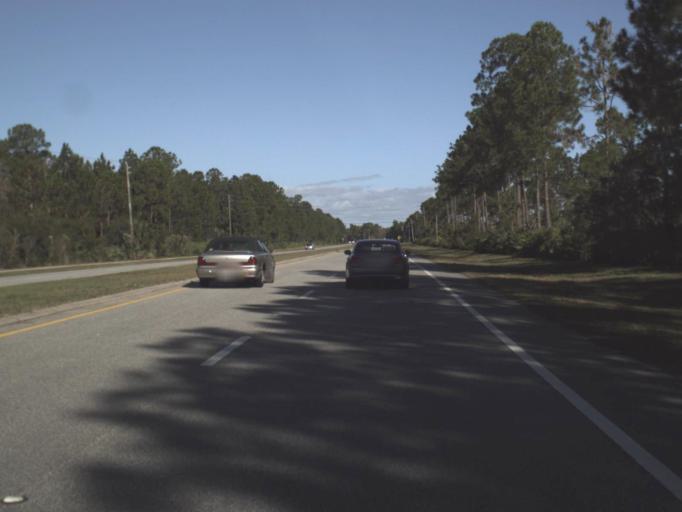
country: US
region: Florida
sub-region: Volusia County
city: Ormond Beach
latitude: 29.2546
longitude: -81.0937
